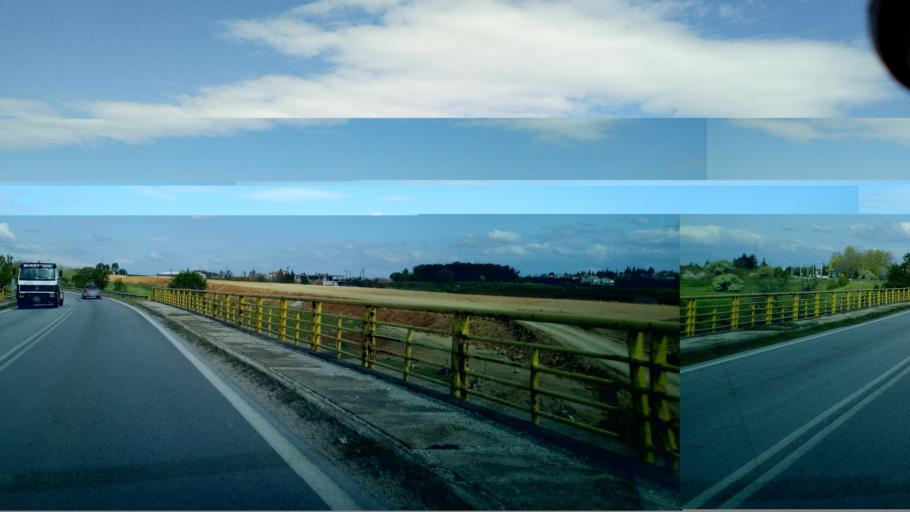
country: GR
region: Central Macedonia
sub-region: Nomos Kilkis
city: Nea Santa
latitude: 40.8312
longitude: 22.9197
